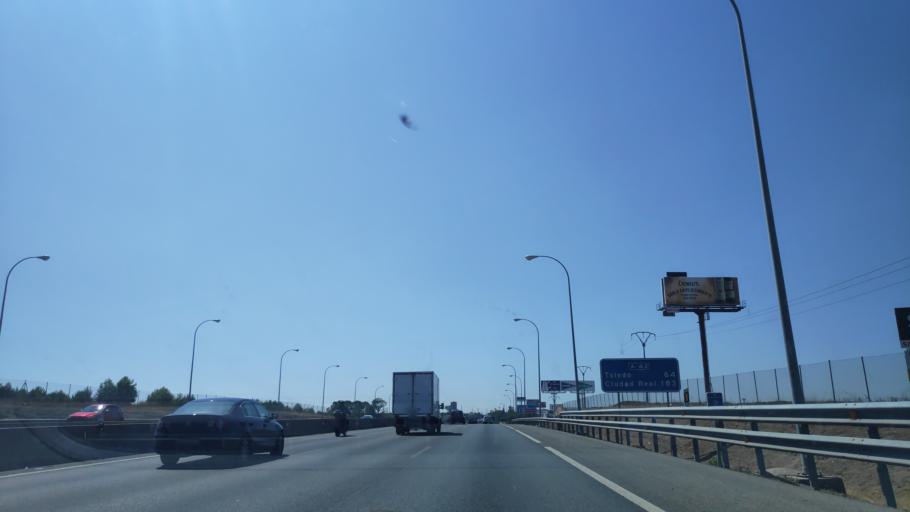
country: ES
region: Madrid
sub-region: Provincia de Madrid
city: Villaverde
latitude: 40.3569
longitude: -3.7219
